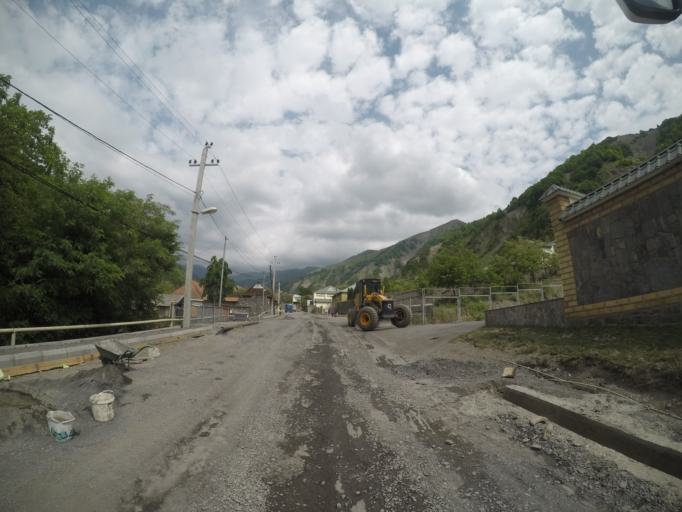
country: AZ
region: Qakh Rayon
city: Qaxbas
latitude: 41.4678
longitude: 47.0595
